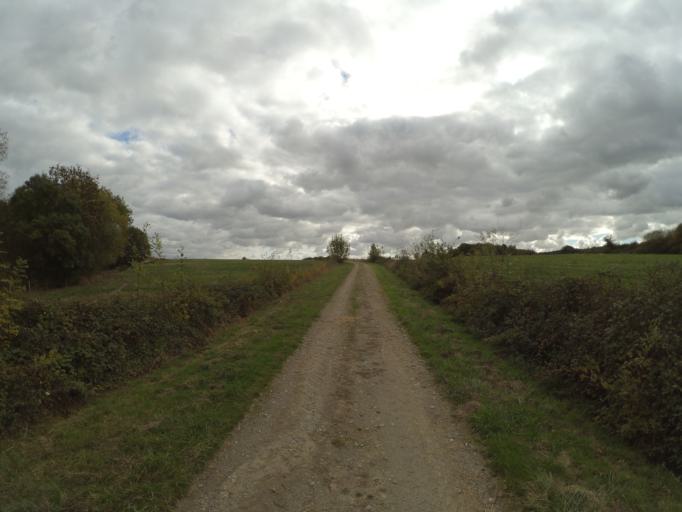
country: FR
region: Pays de la Loire
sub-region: Departement de la Loire-Atlantique
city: Remouille
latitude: 47.0523
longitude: -1.3567
